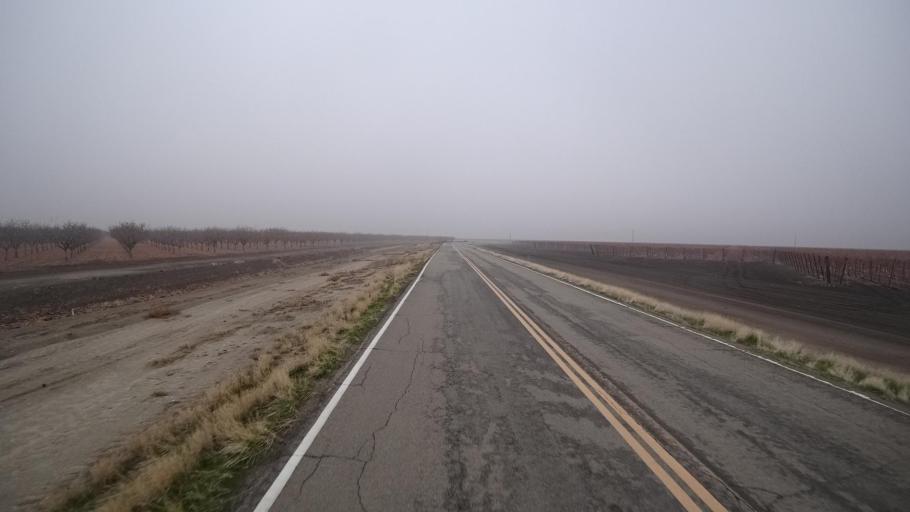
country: US
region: California
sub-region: Kern County
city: Buttonwillow
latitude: 35.4243
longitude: -119.5308
